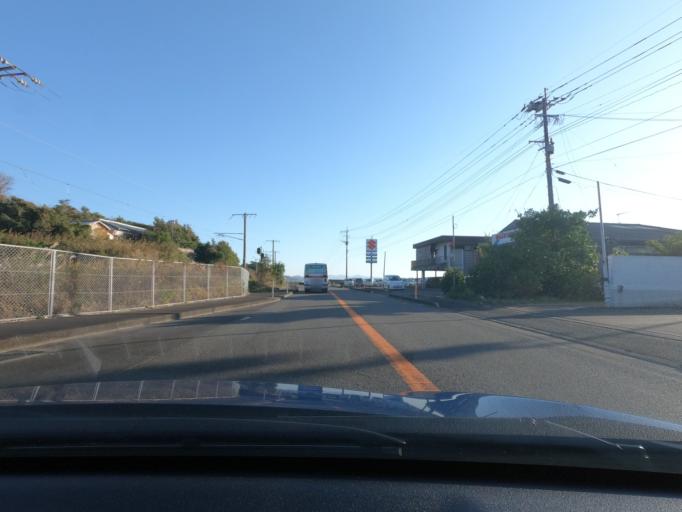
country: JP
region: Kagoshima
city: Akune
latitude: 31.9775
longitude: 130.2041
